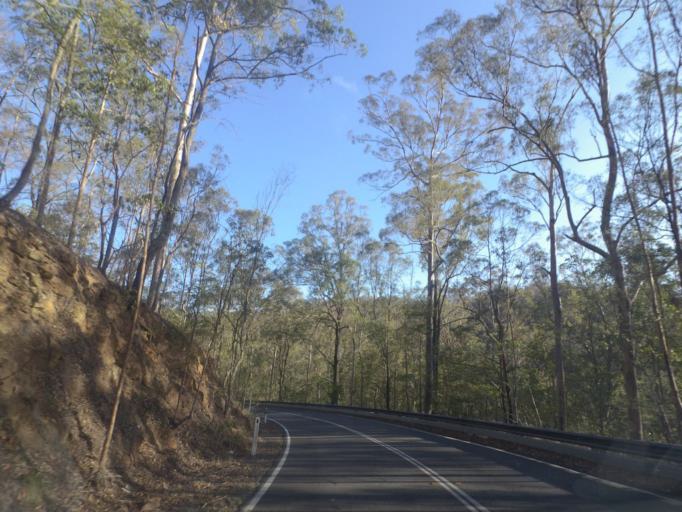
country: AU
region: Queensland
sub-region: Brisbane
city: Taringa
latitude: -27.4644
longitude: 152.9630
